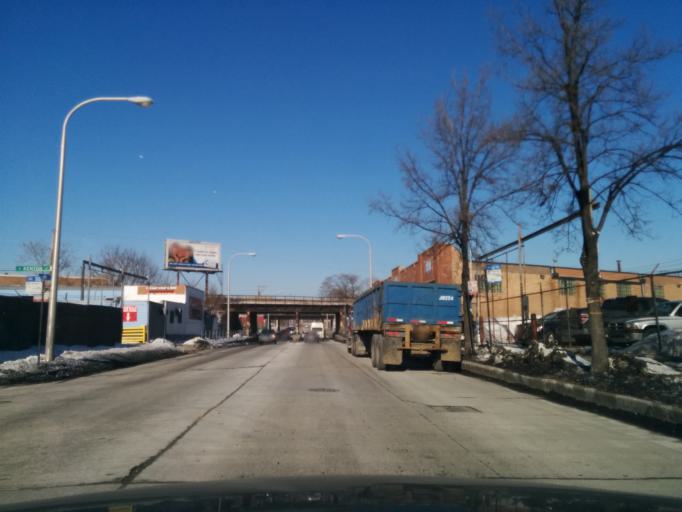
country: US
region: Illinois
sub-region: Cook County
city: Oak Park
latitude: 41.9116
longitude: -87.7401
